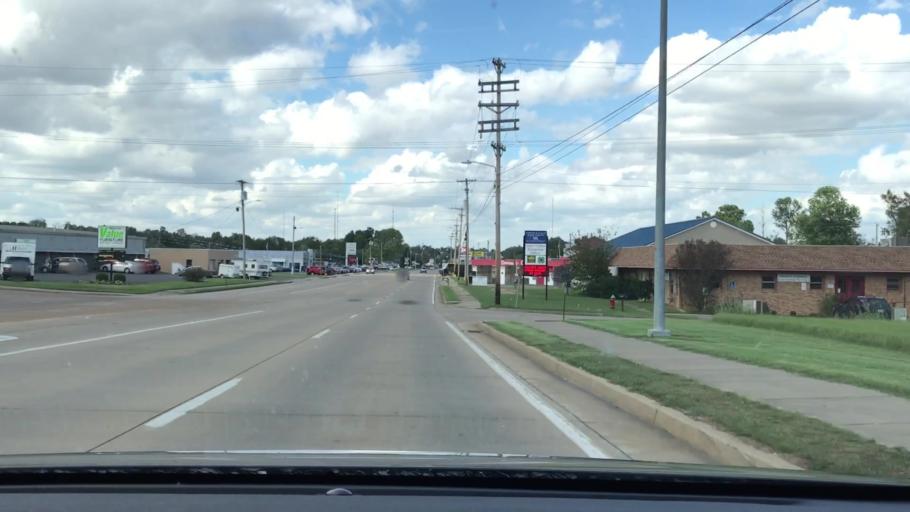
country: US
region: Kentucky
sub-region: Graves County
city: Mayfield
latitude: 36.7515
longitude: -88.6385
